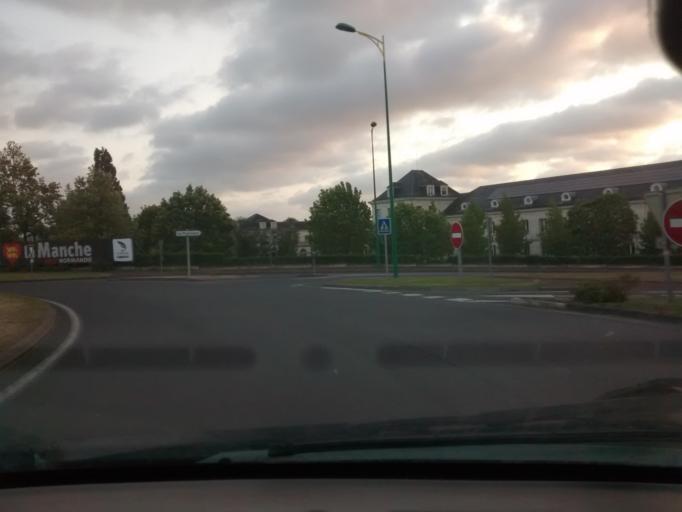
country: FR
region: Lower Normandy
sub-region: Departement de la Manche
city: Agneaux
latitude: 49.1016
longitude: -1.1162
